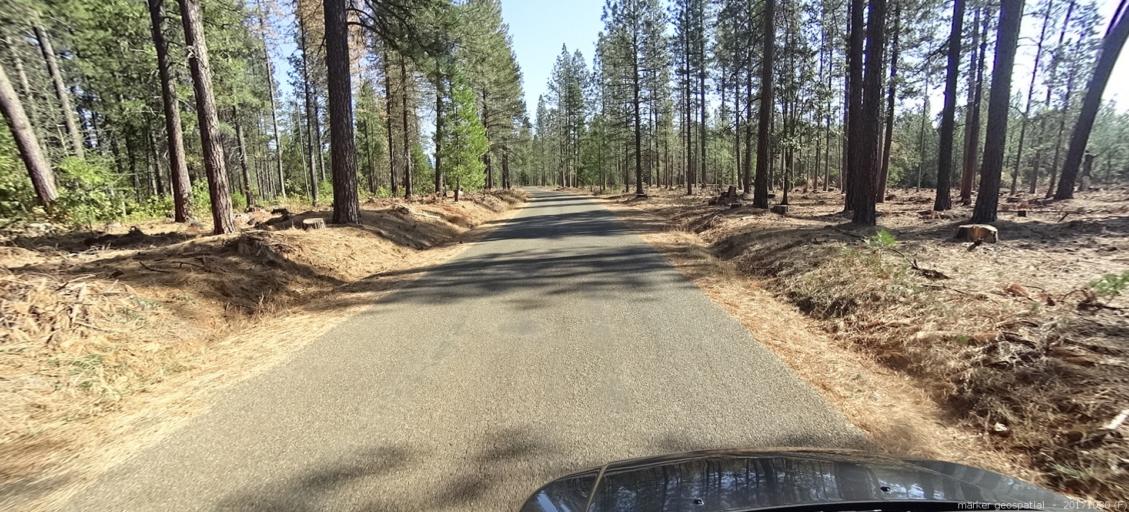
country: US
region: California
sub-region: Shasta County
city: Shingletown
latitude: 40.6103
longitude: -121.8691
